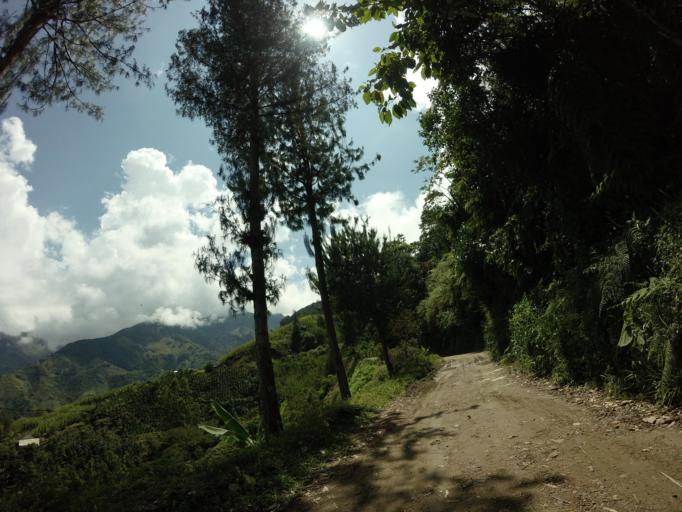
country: CO
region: Caldas
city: Pensilvania
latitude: 5.4731
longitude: -75.1860
